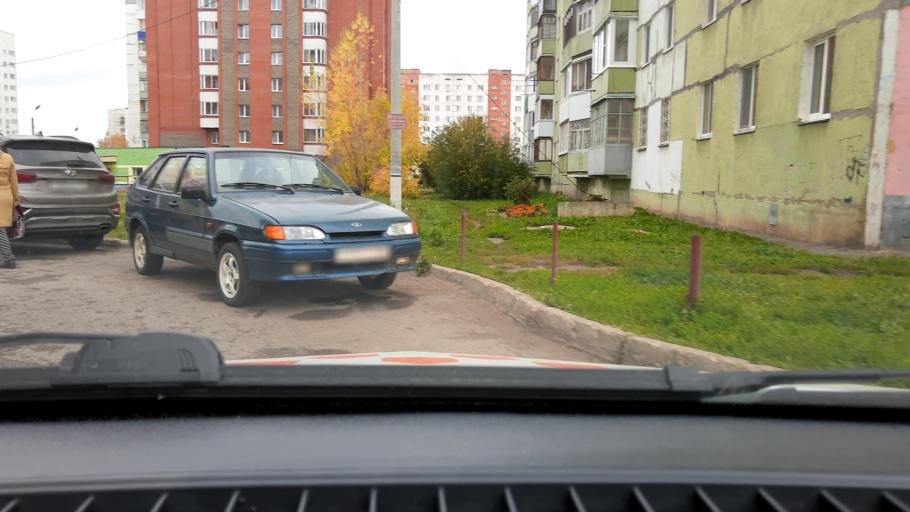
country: RU
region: Bashkortostan
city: Mikhaylovka
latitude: 54.7126
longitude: 55.8327
